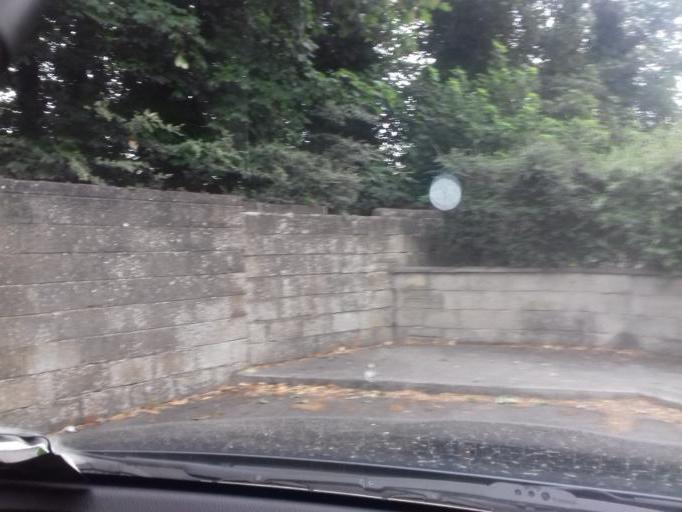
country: IE
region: Leinster
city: Hartstown
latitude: 53.3949
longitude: -6.4105
